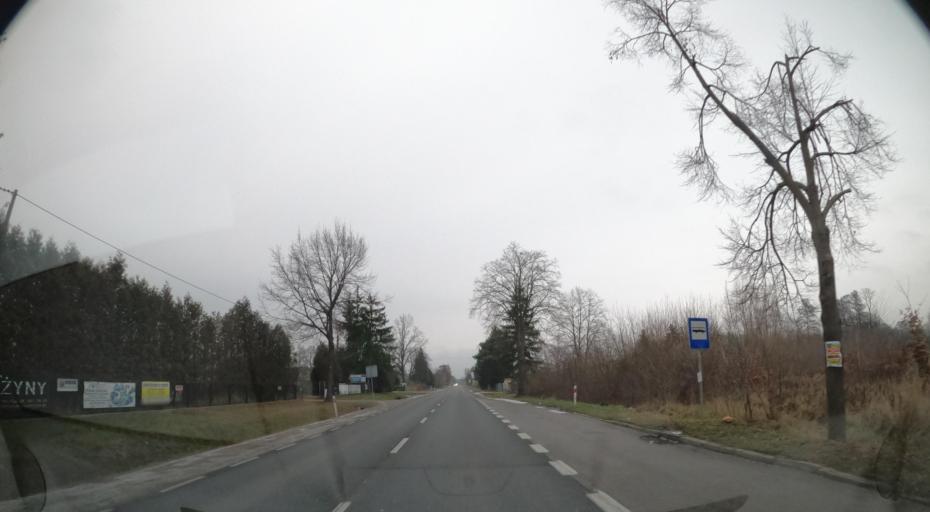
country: PL
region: Masovian Voivodeship
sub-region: Powiat radomski
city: Jastrzebia
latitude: 51.4265
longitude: 21.2272
